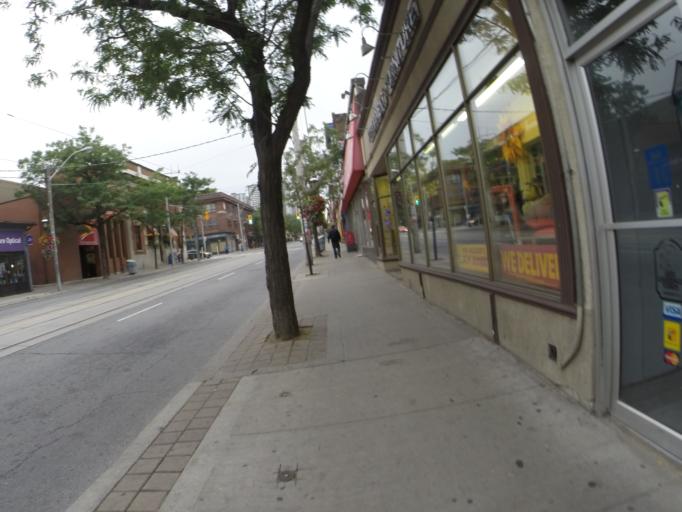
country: CA
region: Ontario
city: Toronto
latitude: 43.6625
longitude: -79.3672
